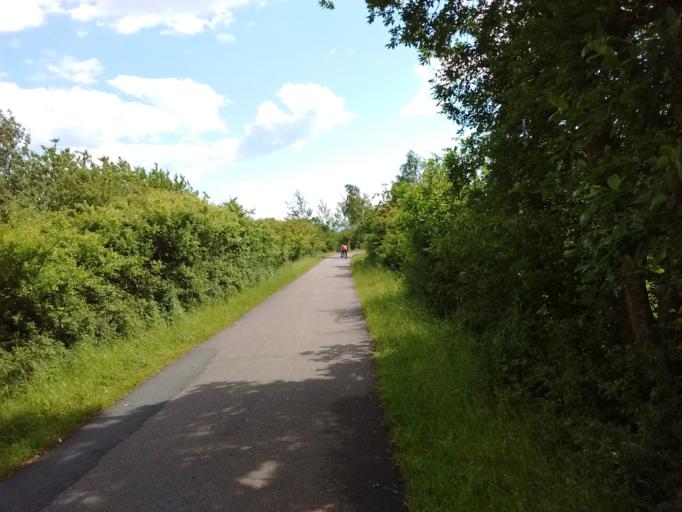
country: DK
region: Capital Region
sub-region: Tarnby Kommune
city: Tarnby
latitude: 55.6057
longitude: 12.5760
